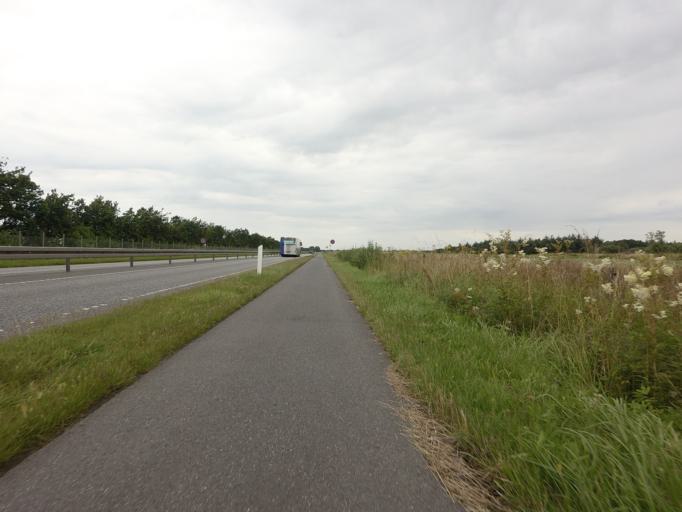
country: DK
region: North Denmark
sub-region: Alborg Kommune
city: Vadum
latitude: 57.0920
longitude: 9.8873
